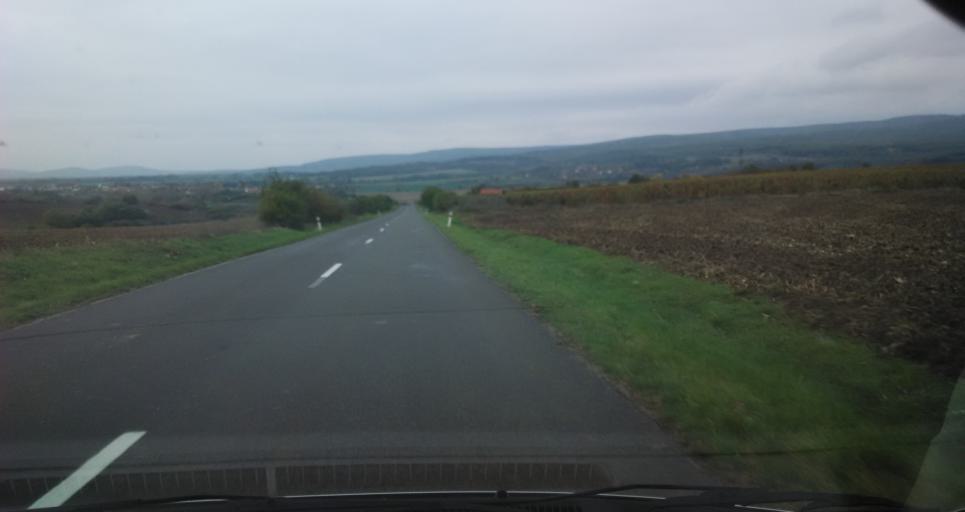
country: SK
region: Nitriansky
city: Levice
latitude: 48.2869
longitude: 18.6831
